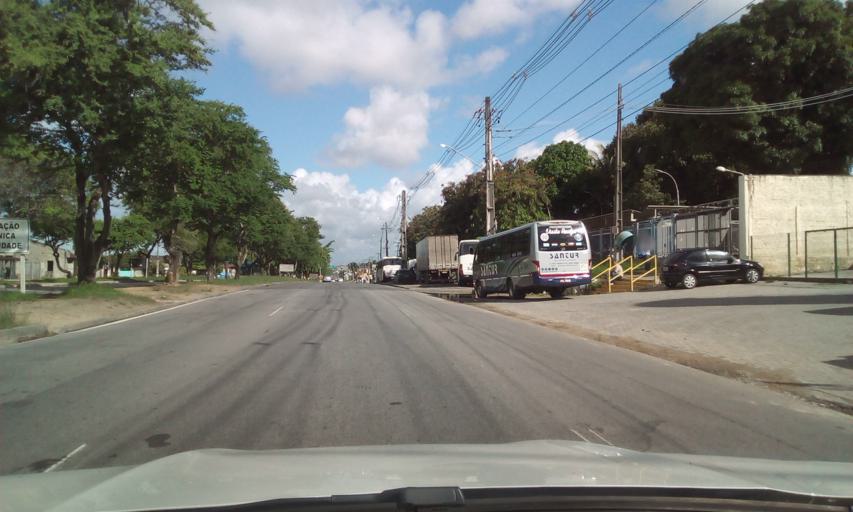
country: BR
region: Pernambuco
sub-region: Igarassu
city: Igarassu
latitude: -7.8597
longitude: -34.9082
